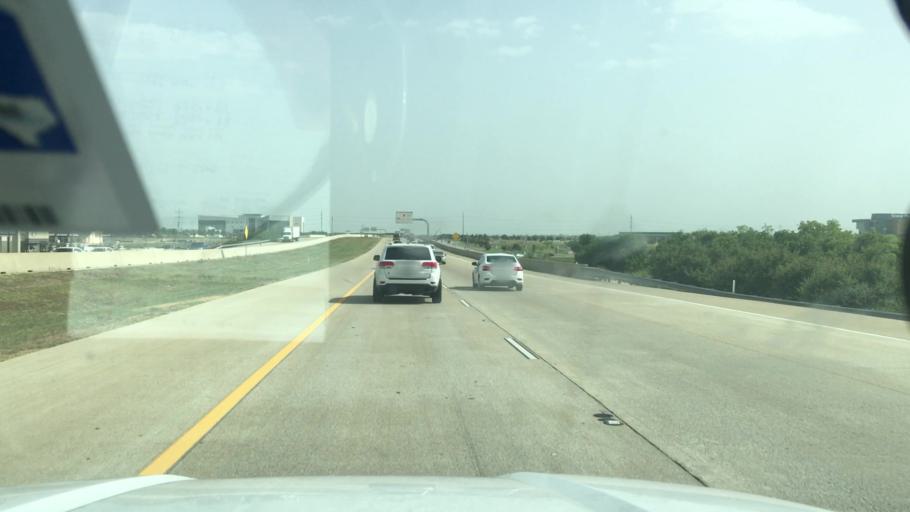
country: US
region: Texas
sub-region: Dallas County
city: Grand Prairie
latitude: 32.7089
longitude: -97.0248
